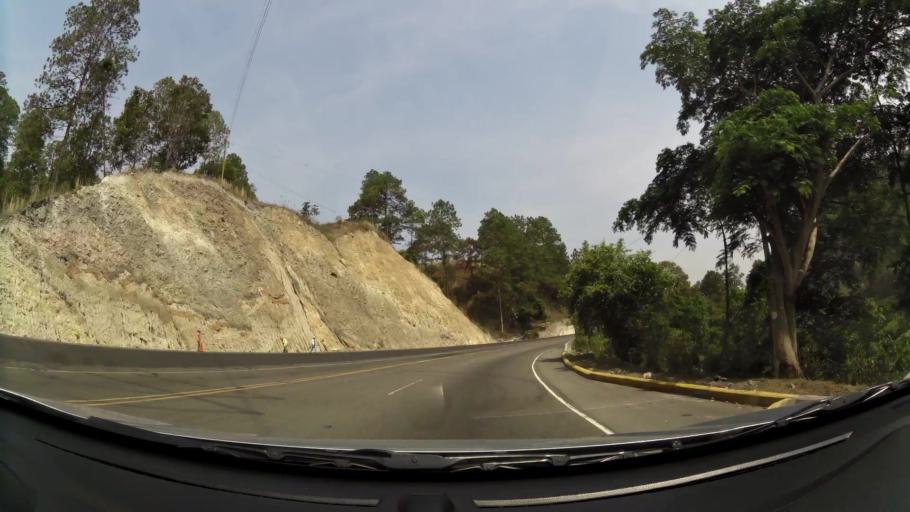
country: HN
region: Comayagua
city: Potrerillos
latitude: 14.5333
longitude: -87.8103
